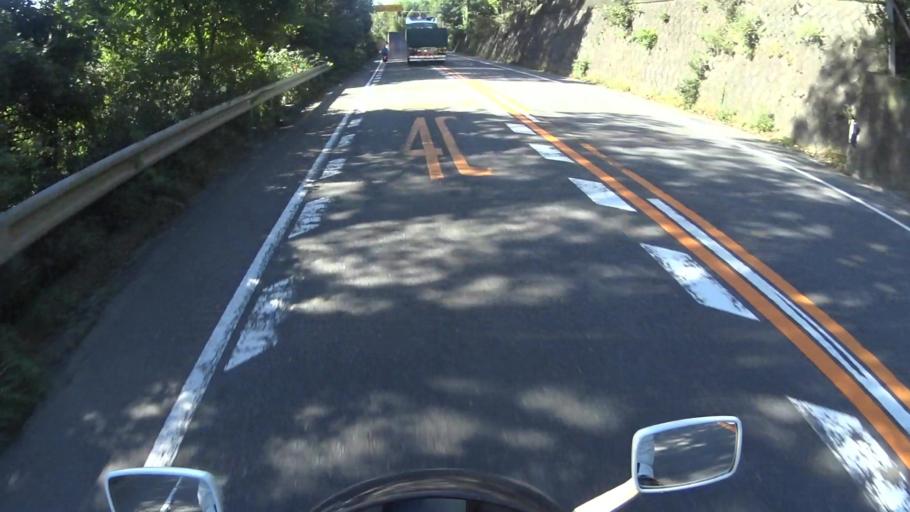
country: JP
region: Kyoto
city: Kameoka
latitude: 34.9927
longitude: 135.6266
